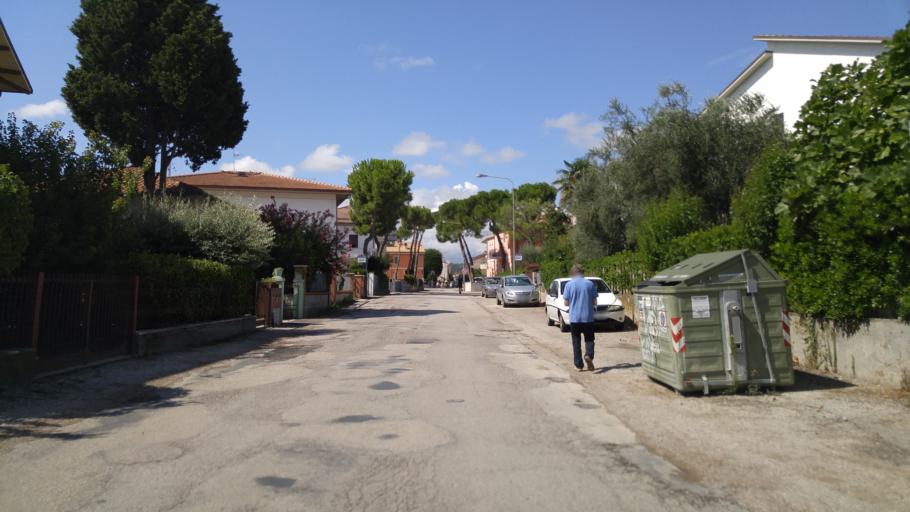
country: IT
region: The Marches
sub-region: Provincia di Pesaro e Urbino
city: Fano
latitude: 43.8374
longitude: 13.0044
